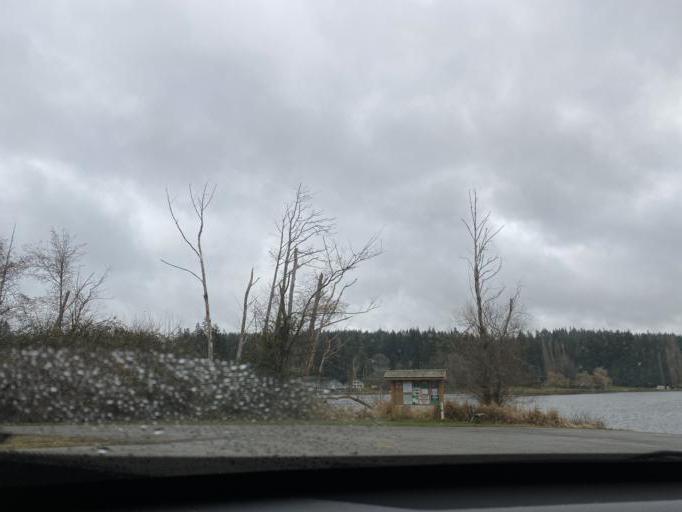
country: US
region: Washington
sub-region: Island County
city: Langley
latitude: 48.0240
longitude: -122.4609
